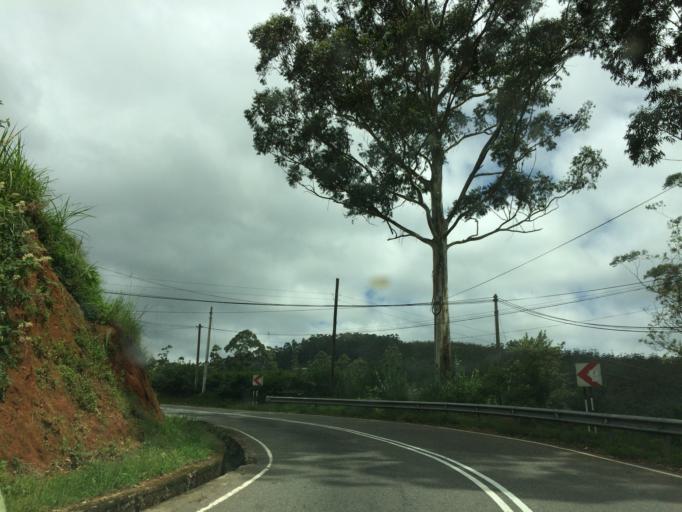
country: LK
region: Central
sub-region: Nuwara Eliya District
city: Nuwara Eliya
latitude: 7.0200
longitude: 80.7260
